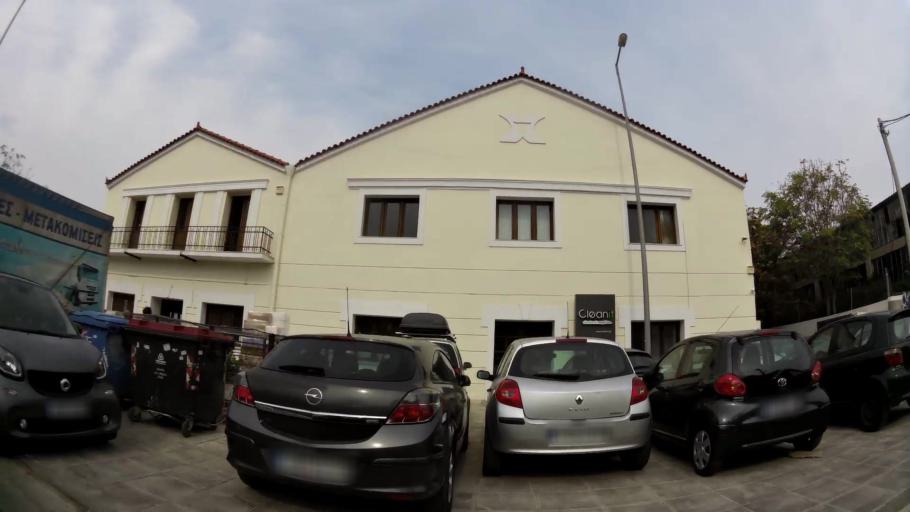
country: GR
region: Attica
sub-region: Nomarchia Athinas
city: Tavros
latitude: 37.9614
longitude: 23.6873
